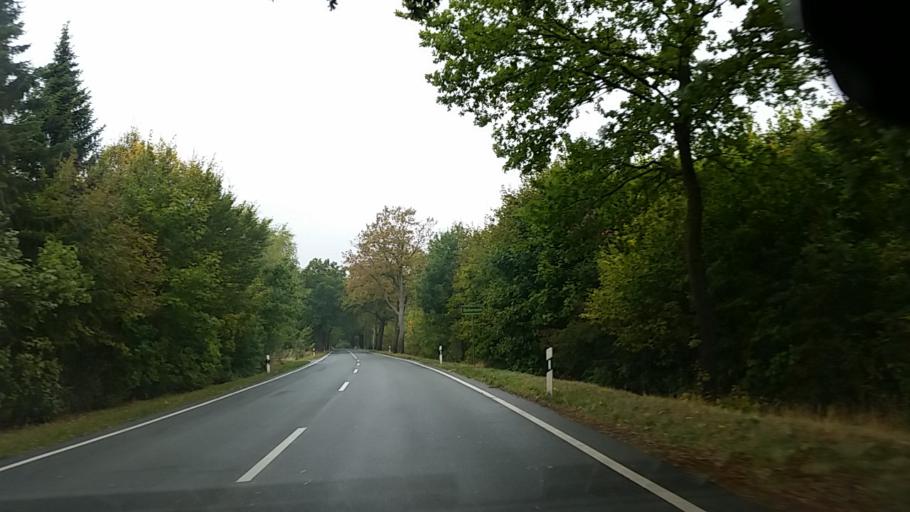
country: DE
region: Lower Saxony
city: Wieren
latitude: 52.8990
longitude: 10.6484
